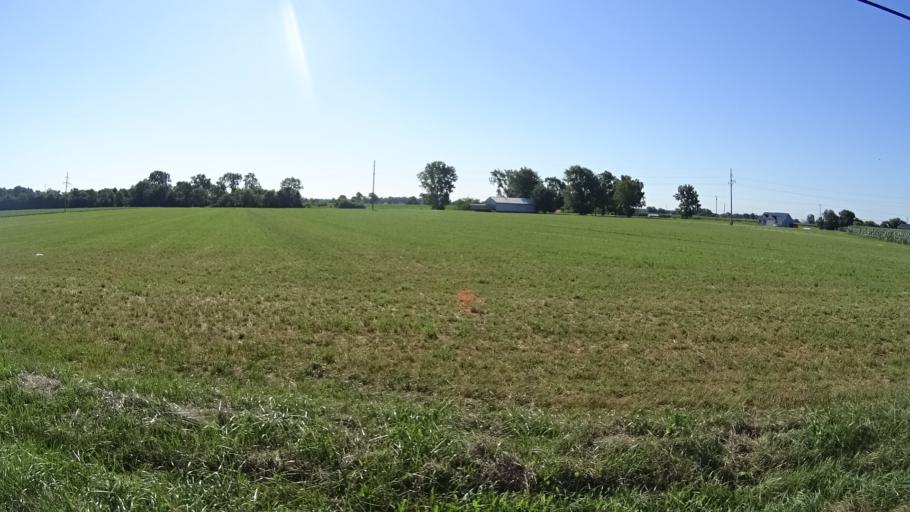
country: US
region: Ohio
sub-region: Erie County
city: Sandusky
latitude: 41.3993
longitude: -82.7505
